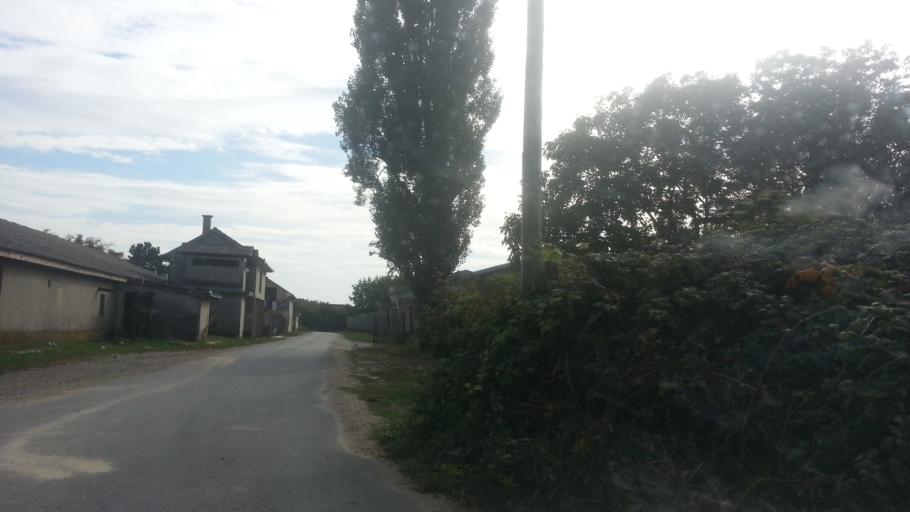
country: RS
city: Belegis
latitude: 45.0107
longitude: 20.3148
